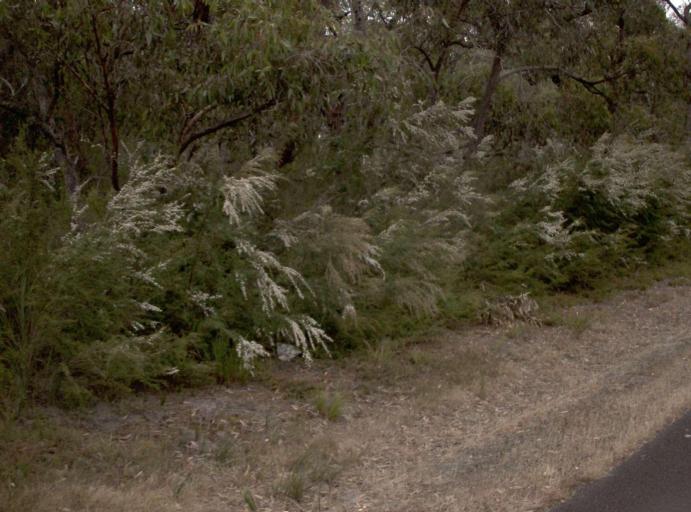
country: AU
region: Victoria
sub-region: Wellington
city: Sale
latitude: -38.3357
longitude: 147.0132
